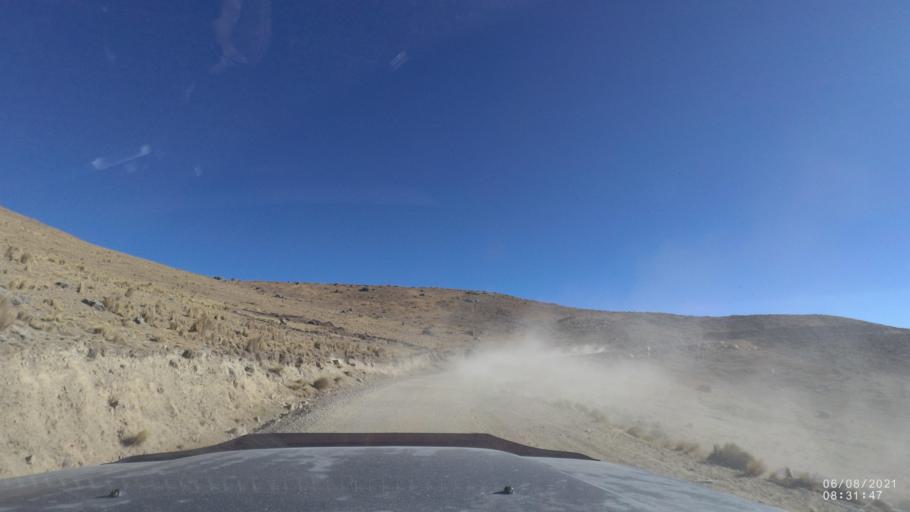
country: BO
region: Cochabamba
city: Sipe Sipe
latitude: -17.1842
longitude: -66.3737
